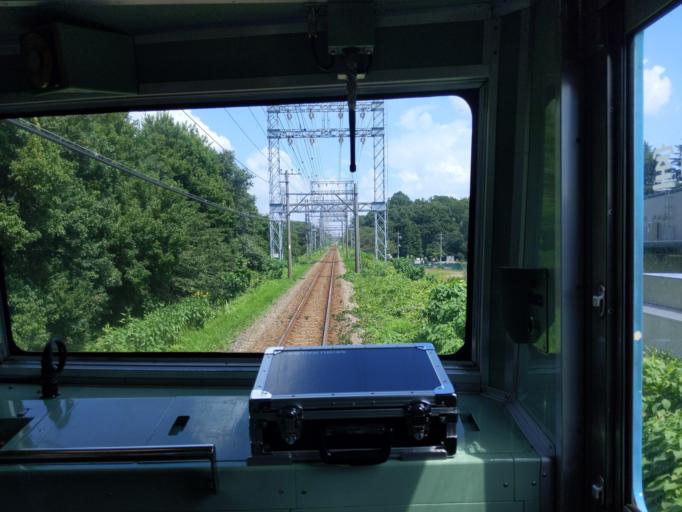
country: JP
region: Tokyo
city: Kamirenjaku
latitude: 35.6868
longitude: 139.5220
